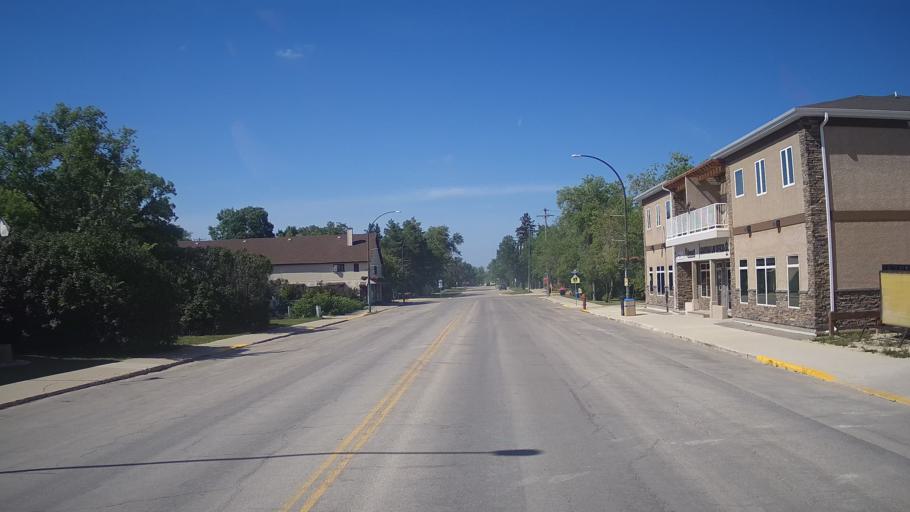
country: CA
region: Manitoba
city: Stonewall
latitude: 50.1365
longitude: -97.3266
